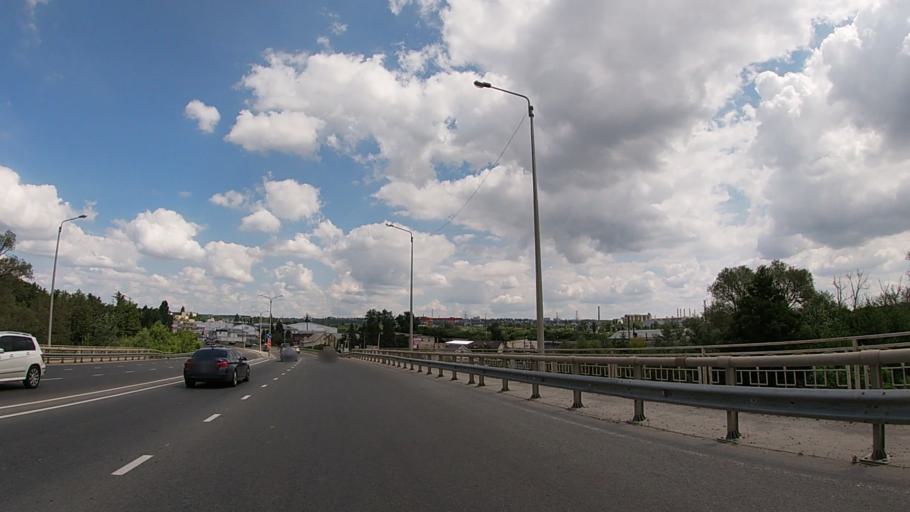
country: RU
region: Belgorod
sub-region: Belgorodskiy Rayon
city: Belgorod
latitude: 50.6075
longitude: 36.5326
